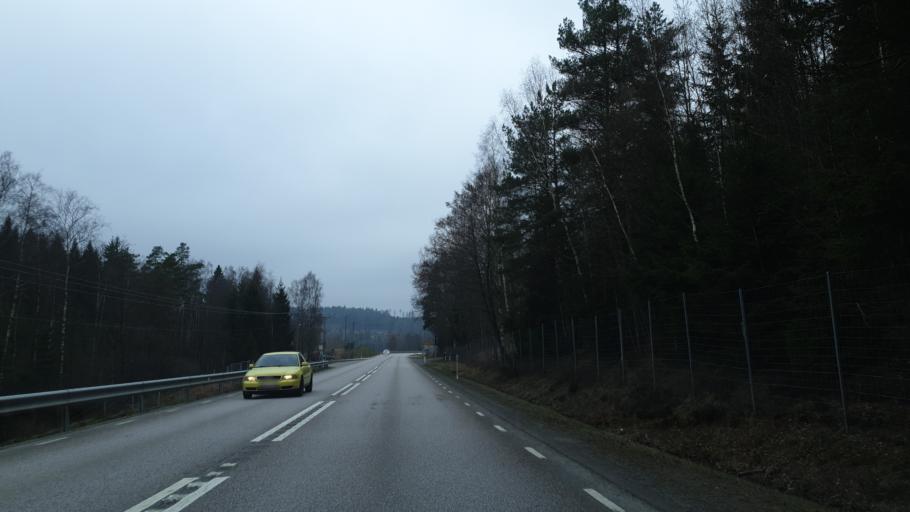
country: SE
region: Vaestra Goetaland
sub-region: Harryda Kommun
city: Hindas
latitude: 57.6244
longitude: 12.4170
